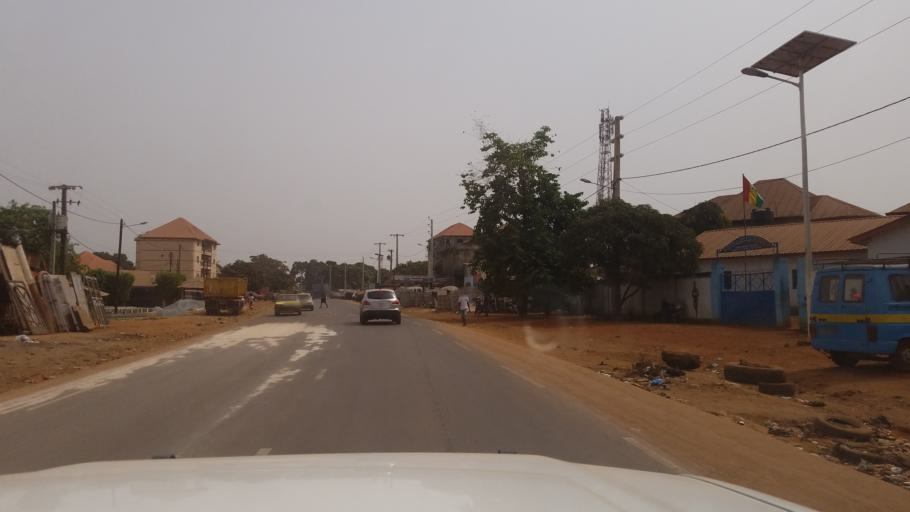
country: GN
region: Kindia
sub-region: Prefecture de Dubreka
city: Dubreka
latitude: 9.6690
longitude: -13.5860
